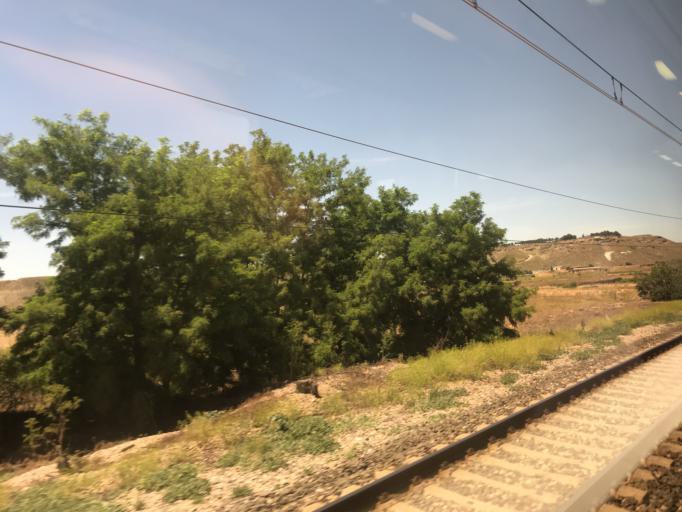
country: ES
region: Madrid
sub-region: Provincia de Madrid
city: Aranjuez
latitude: 40.0601
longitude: -3.6364
